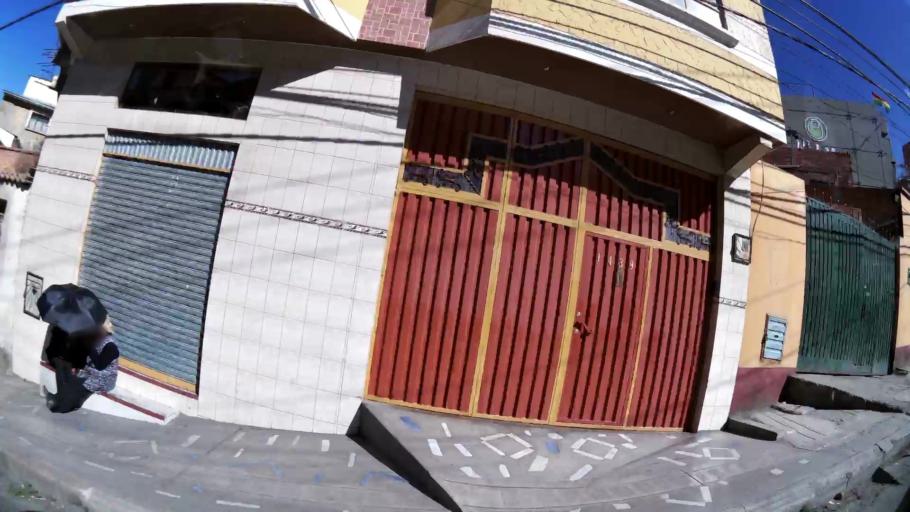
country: BO
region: La Paz
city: La Paz
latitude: -16.5104
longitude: -68.1455
